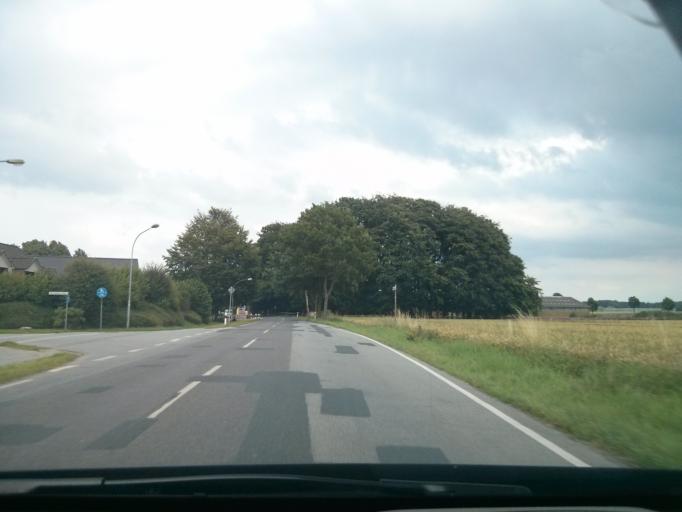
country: DE
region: Lower Saxony
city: Bendestorf
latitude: 53.3641
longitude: 9.9375
